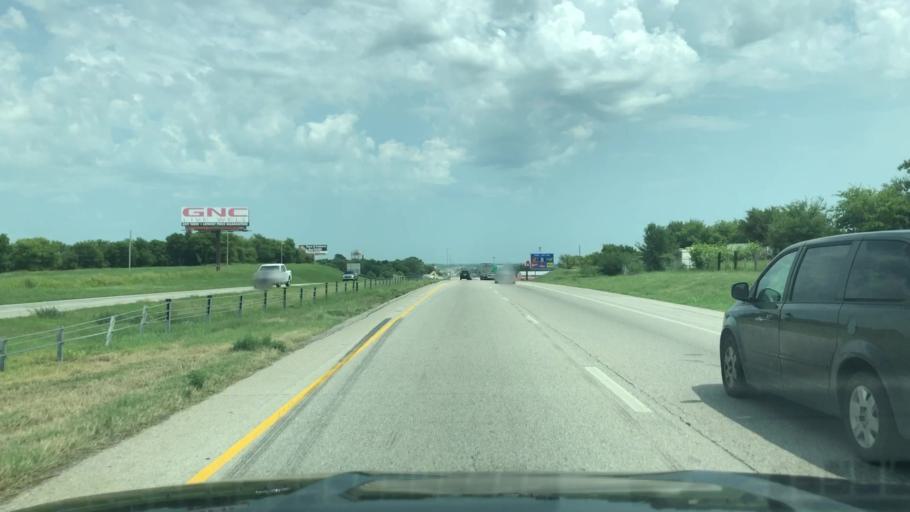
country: US
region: Oklahoma
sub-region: Rogers County
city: Catoosa
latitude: 36.1625
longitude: -95.7866
